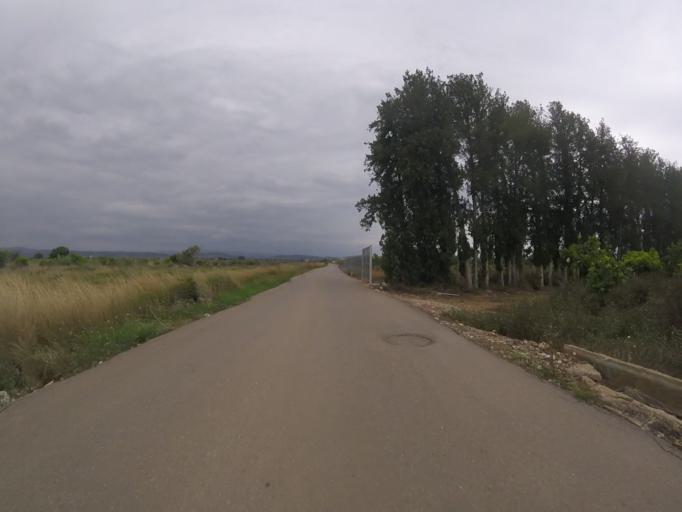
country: ES
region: Valencia
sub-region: Provincia de Castello
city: Alcoceber
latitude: 40.2112
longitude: 0.2503
